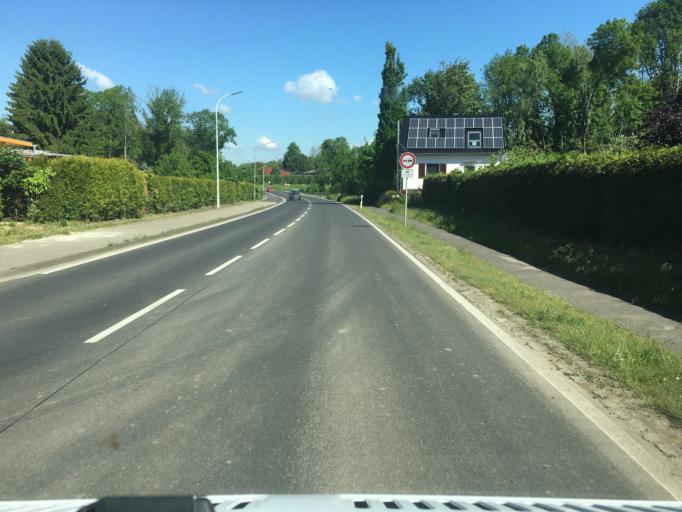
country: DE
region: North Rhine-Westphalia
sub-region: Regierungsbezirk Koln
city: Linnich
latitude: 50.9646
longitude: 6.3204
